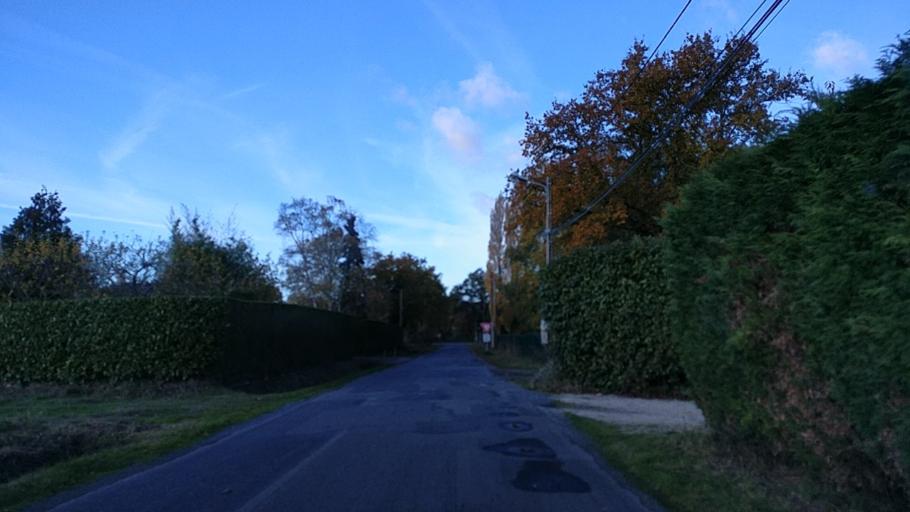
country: FR
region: Brittany
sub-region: Departement d'Ille-et-Vilaine
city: Fouillard
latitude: 48.1392
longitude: -1.5708
